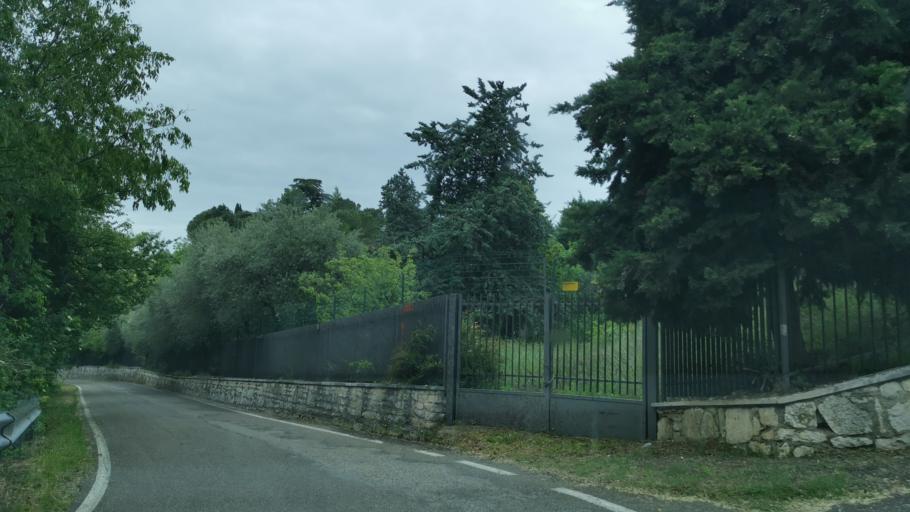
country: IT
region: Veneto
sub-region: Provincia di Verona
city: Cavajon Veronese
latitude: 45.5387
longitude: 10.7532
